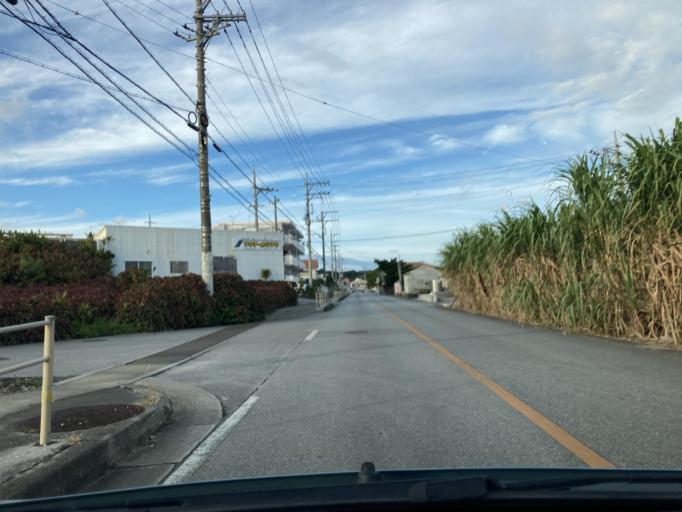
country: JP
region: Okinawa
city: Itoman
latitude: 26.1412
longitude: 127.6886
